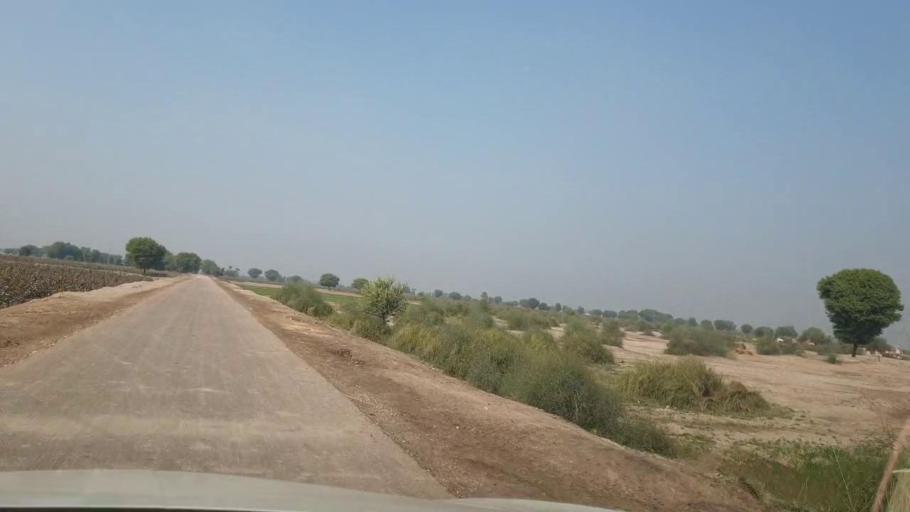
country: PK
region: Sindh
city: Bhan
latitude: 26.5352
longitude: 67.7483
